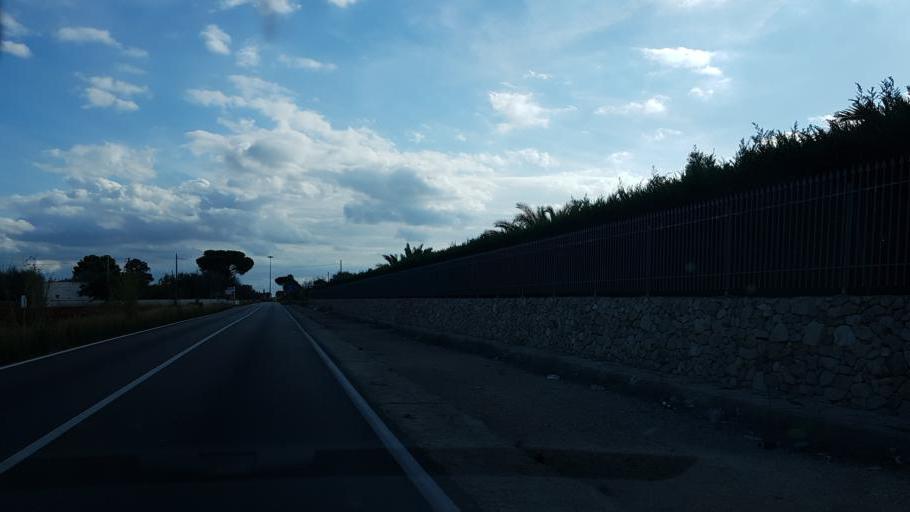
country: IT
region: Apulia
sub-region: Provincia di Lecce
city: Nardo
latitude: 40.1321
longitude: 18.0192
